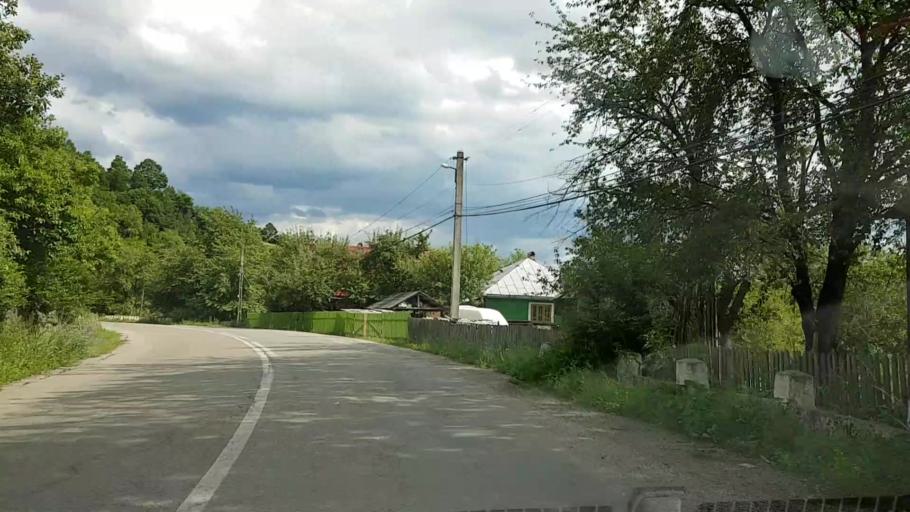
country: RO
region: Neamt
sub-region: Comuna Hangu
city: Hangu
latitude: 47.0296
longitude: 26.0658
